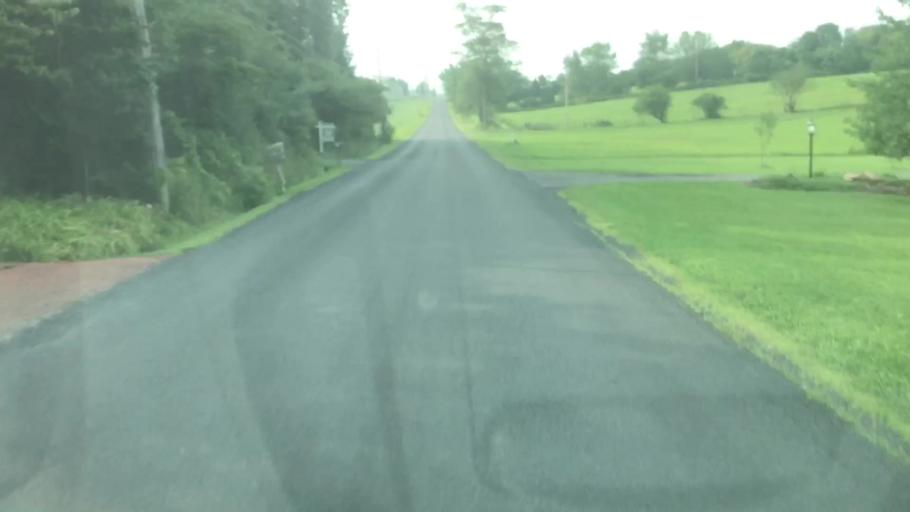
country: US
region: New York
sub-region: Onondaga County
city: Skaneateles
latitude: 42.9327
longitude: -76.4577
